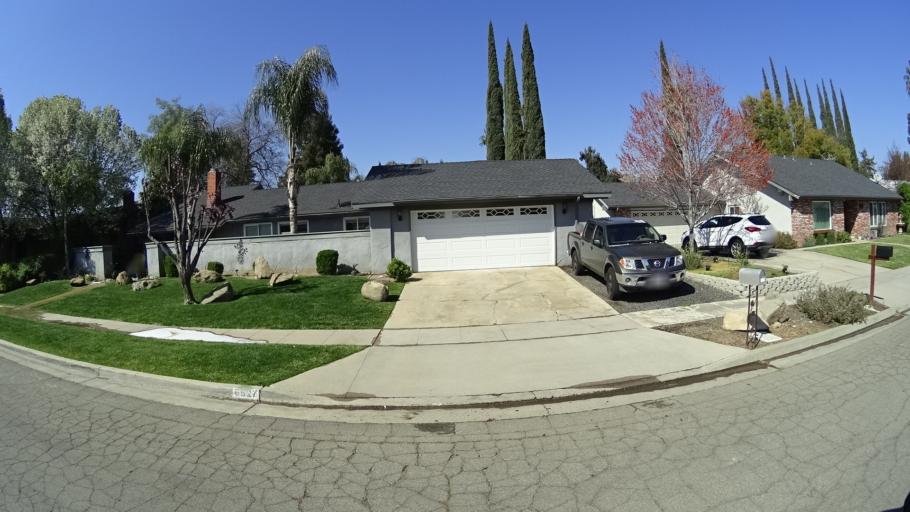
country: US
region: California
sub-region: Fresno County
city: Clovis
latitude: 36.8307
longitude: -119.7311
